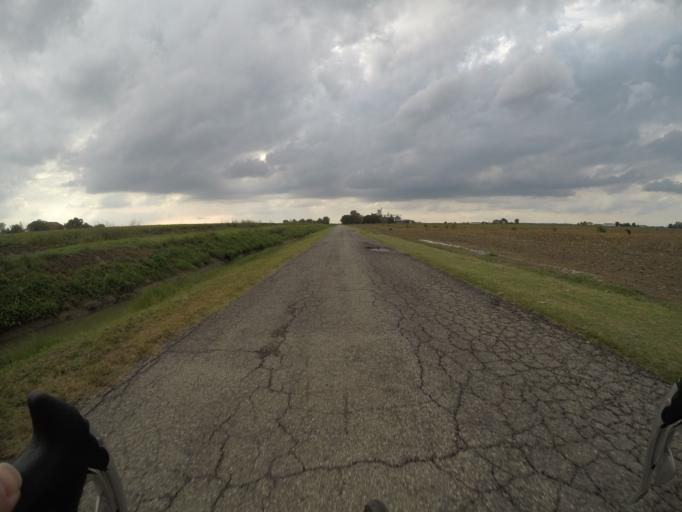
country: IT
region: Veneto
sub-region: Provincia di Rovigo
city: Polesella
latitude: 44.9661
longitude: 11.7293
